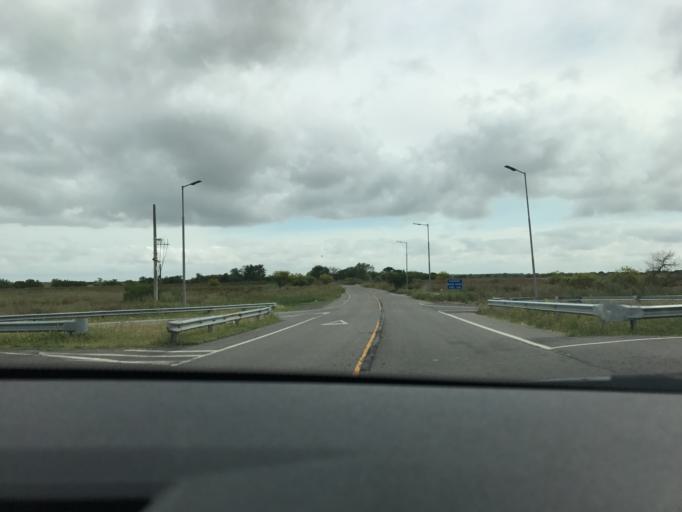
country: AR
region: Buenos Aires
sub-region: Partido de La Plata
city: La Plata
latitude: -34.8375
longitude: -58.0689
